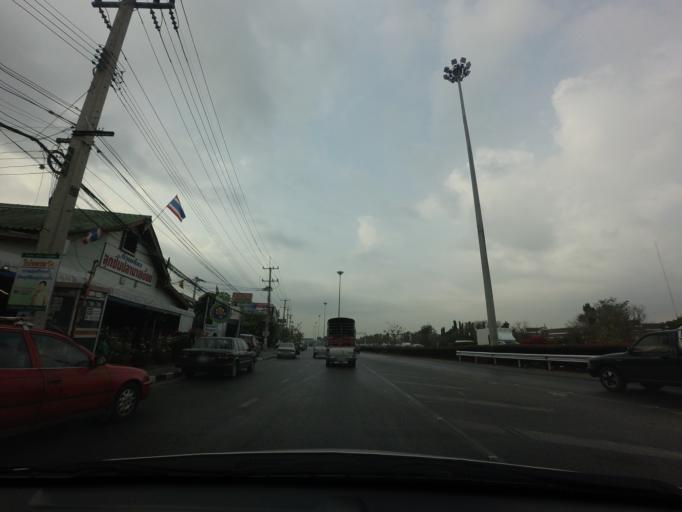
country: TH
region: Bangkok
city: Thawi Watthana
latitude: 13.7847
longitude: 100.3280
